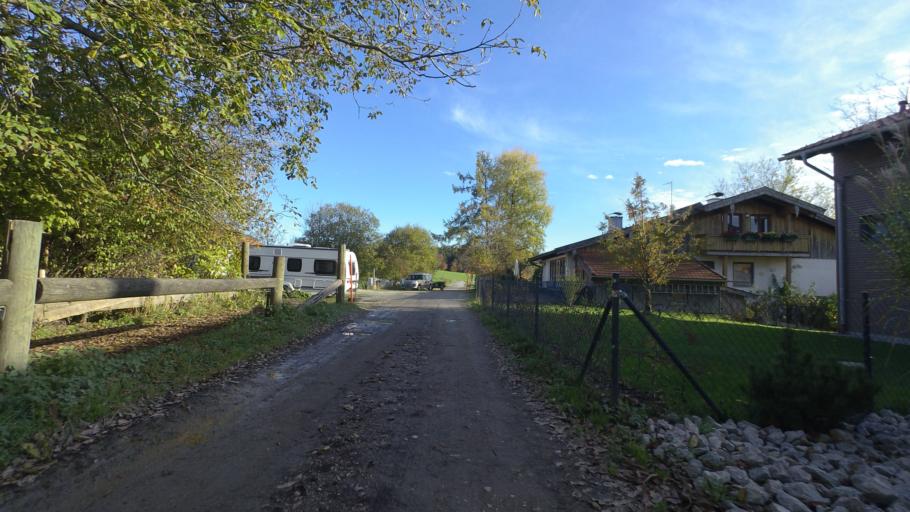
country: DE
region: Bavaria
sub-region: Upper Bavaria
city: Nussdorf
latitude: 47.9200
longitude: 12.5685
